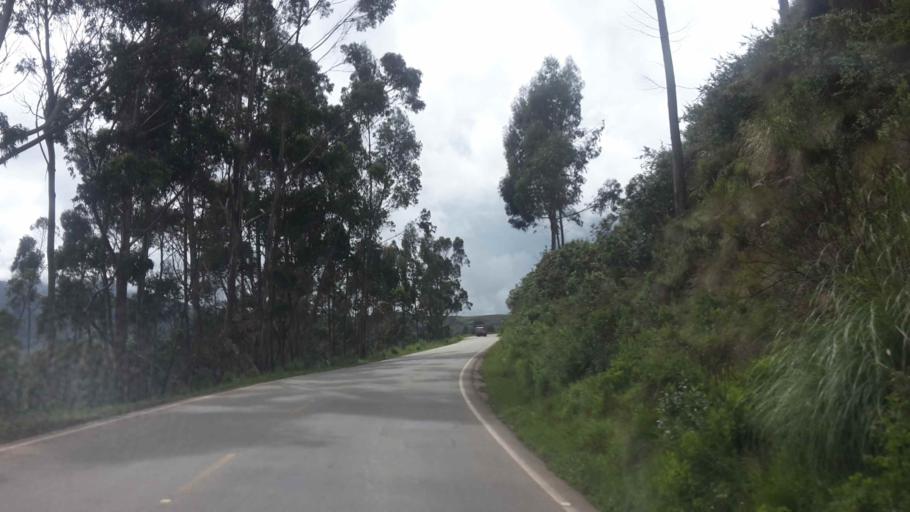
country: BO
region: Cochabamba
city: Totora
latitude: -17.5543
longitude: -65.3470
